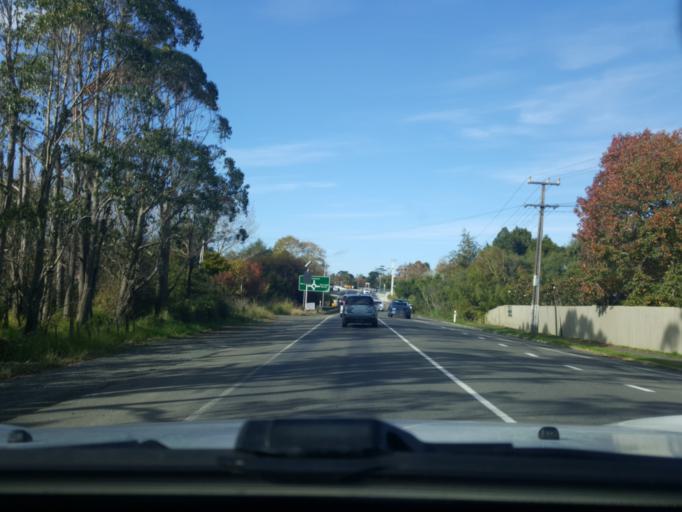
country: NZ
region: Auckland
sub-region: Auckland
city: Muriwai Beach
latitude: -36.7694
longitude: 174.4886
